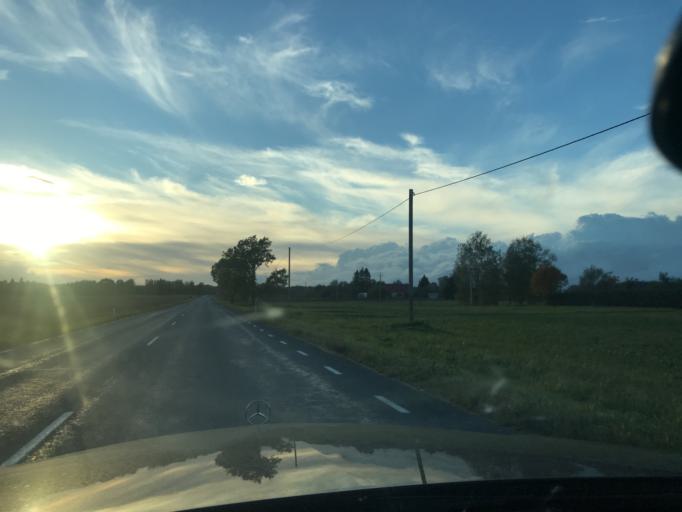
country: EE
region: Vorumaa
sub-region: Antsla vald
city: Vana-Antsla
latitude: 57.8798
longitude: 26.7164
